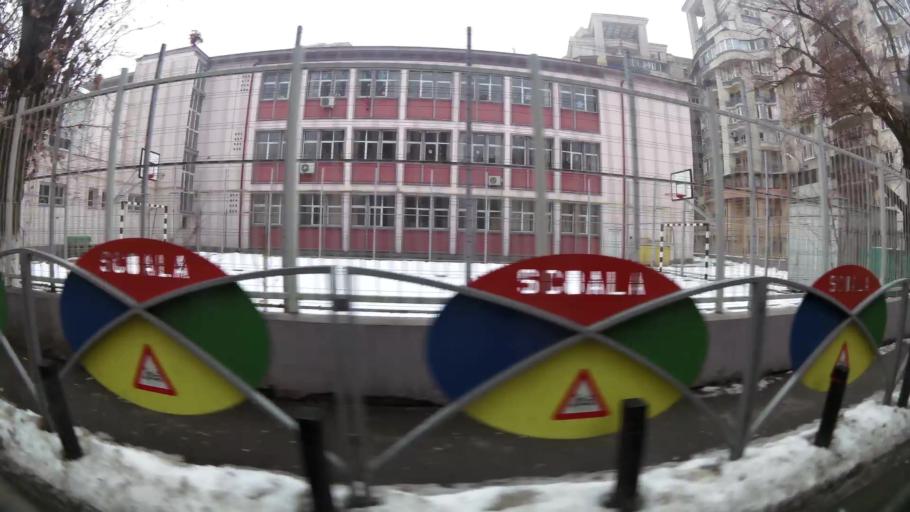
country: RO
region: Bucuresti
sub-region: Municipiul Bucuresti
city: Bucharest
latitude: 44.4269
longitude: 26.1241
